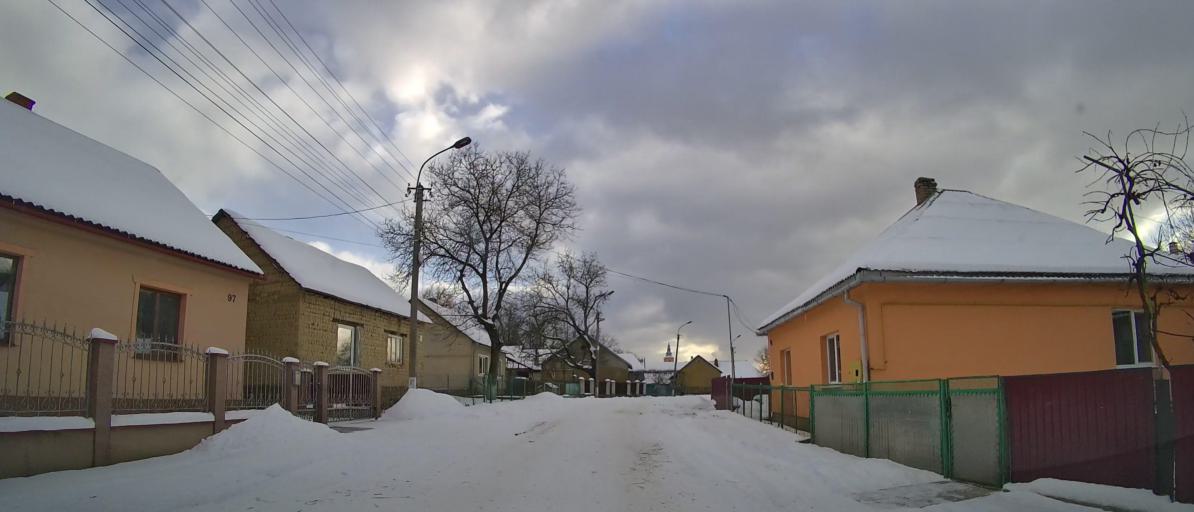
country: UA
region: Zakarpattia
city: Velykyi Bereznyi
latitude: 48.9202
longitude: 22.4640
